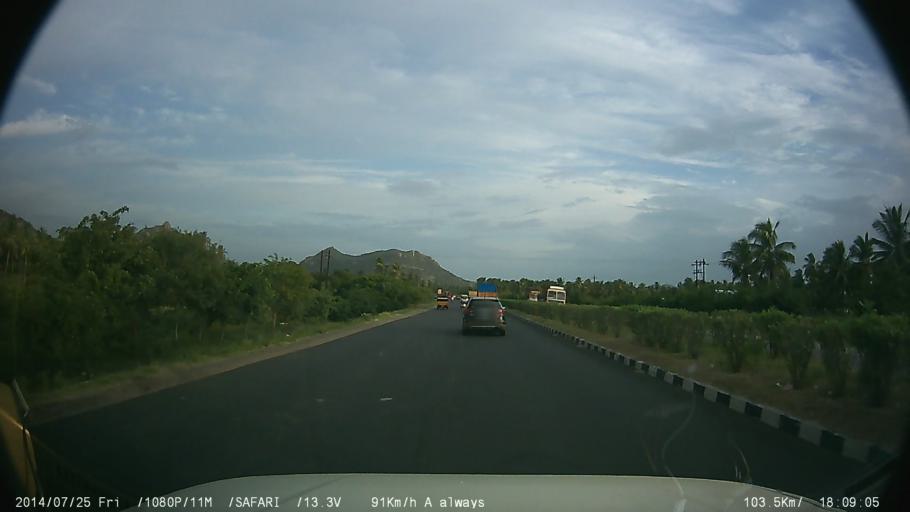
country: IN
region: Tamil Nadu
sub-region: Krishnagiri
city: Kaverippattanam
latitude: 12.3935
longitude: 78.2188
